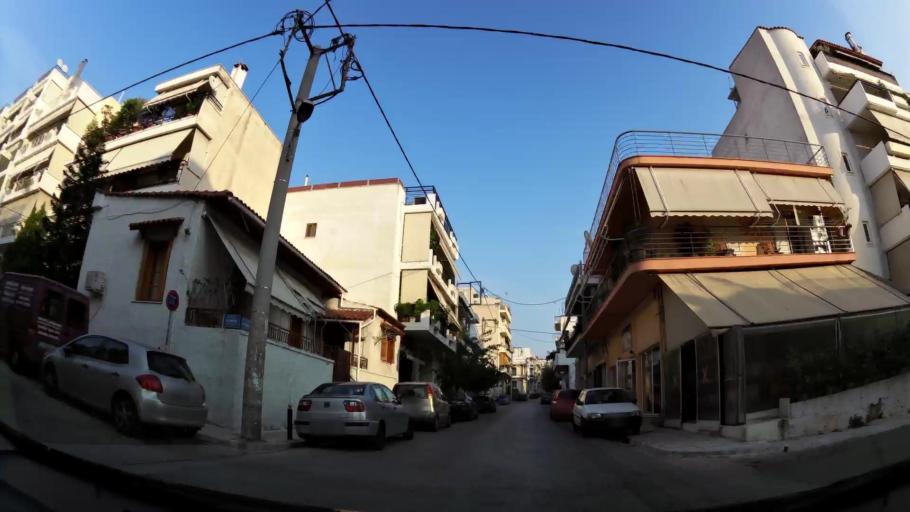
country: GR
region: Attica
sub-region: Nomarchia Athinas
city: Nea Filadelfeia
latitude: 38.0280
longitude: 23.7454
